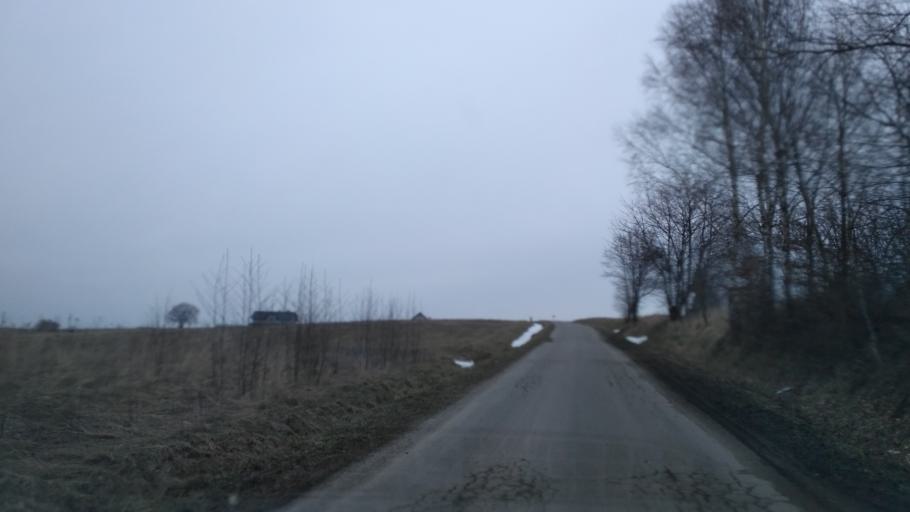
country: PL
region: Subcarpathian Voivodeship
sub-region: Powiat rzeszowski
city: Chmielnik
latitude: 49.9825
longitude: 22.1528
